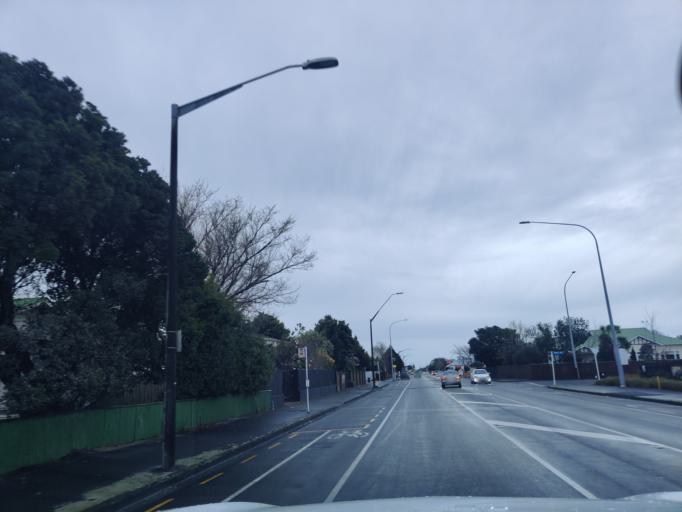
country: NZ
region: Manawatu-Wanganui
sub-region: Palmerston North City
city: Palmerston North
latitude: -40.3469
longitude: 175.6130
